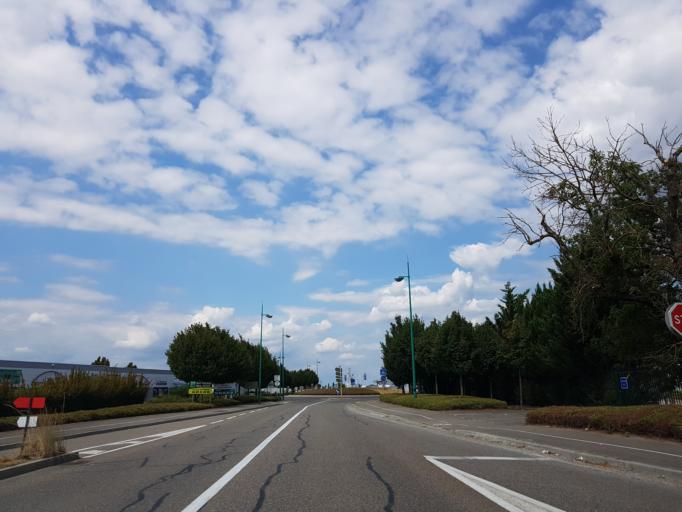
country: FR
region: Alsace
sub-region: Departement du Haut-Rhin
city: Sausheim
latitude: 47.7852
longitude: 7.3883
